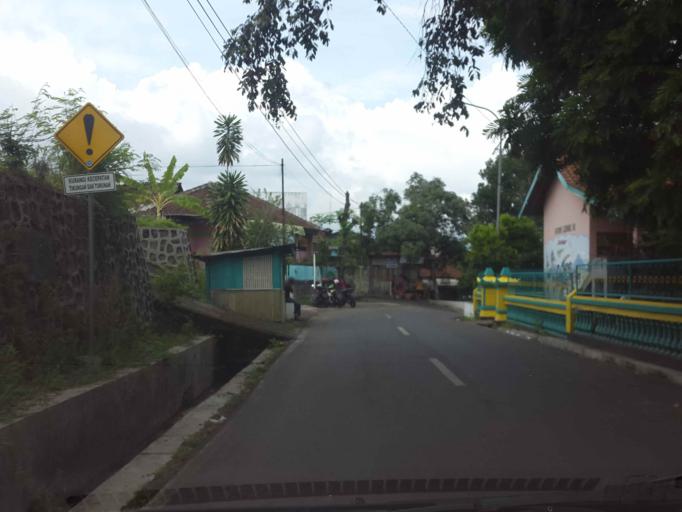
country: ID
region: Central Java
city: Salatiga
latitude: -7.3424
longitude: 110.5113
